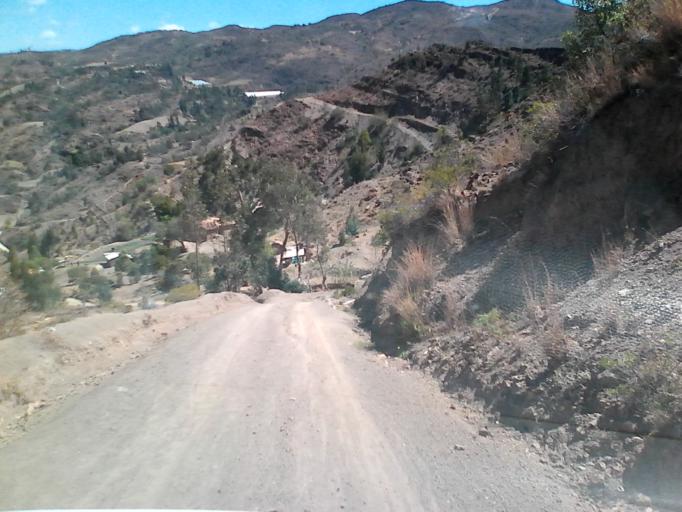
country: CO
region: Boyaca
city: Sachica
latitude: 5.5431
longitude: -73.5352
